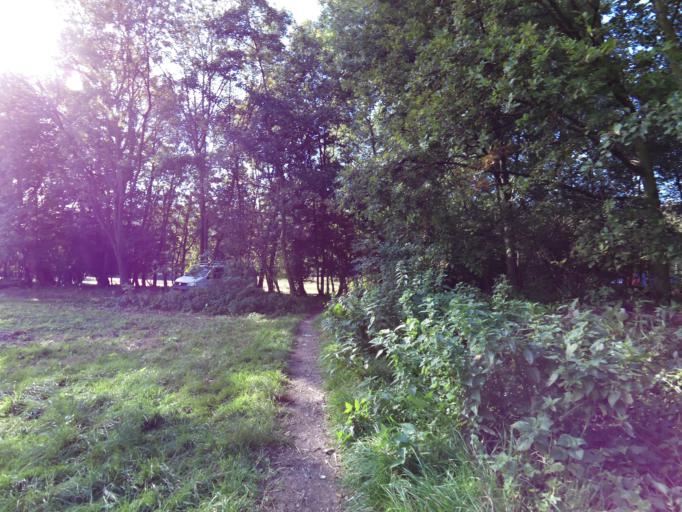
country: NL
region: South Holland
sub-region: Gemeente Vlaardingen
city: Vlaardingen
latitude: 51.9263
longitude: 4.3385
